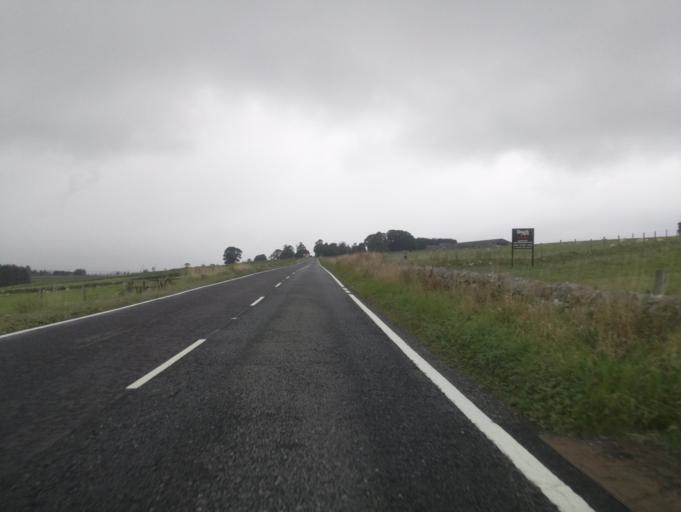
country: GB
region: England
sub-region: Northumberland
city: Otterburn
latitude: 55.2249
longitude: -2.1477
